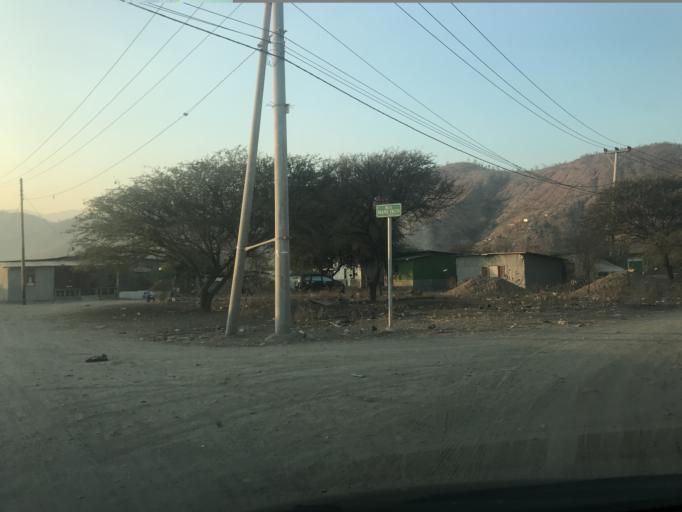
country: TL
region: Dili
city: Dili
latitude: -8.5577
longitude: 125.4984
